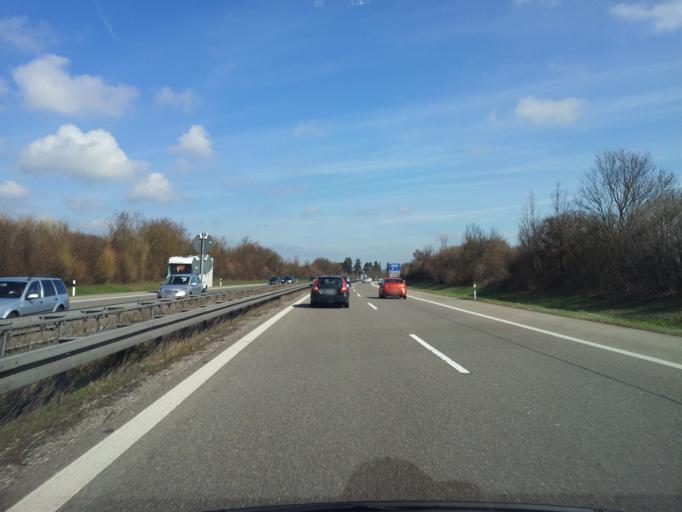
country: DE
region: Baden-Wuerttemberg
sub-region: Freiburg Region
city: Vohringen
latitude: 48.3339
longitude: 8.6468
